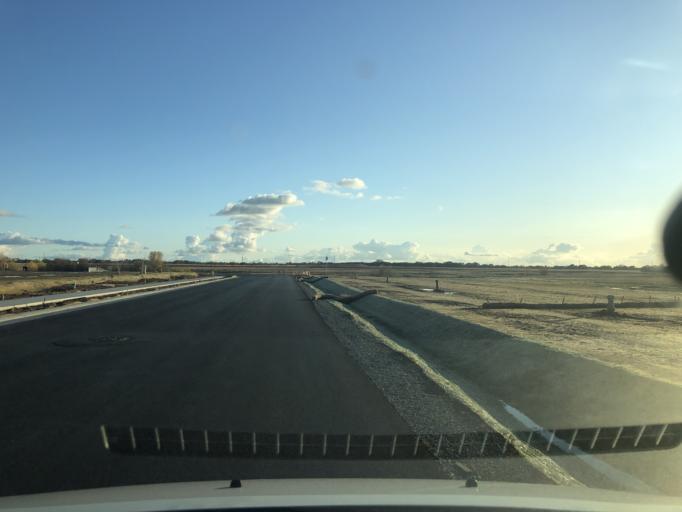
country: US
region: California
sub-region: Sacramento County
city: Antelope
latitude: 38.7571
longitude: -121.3679
